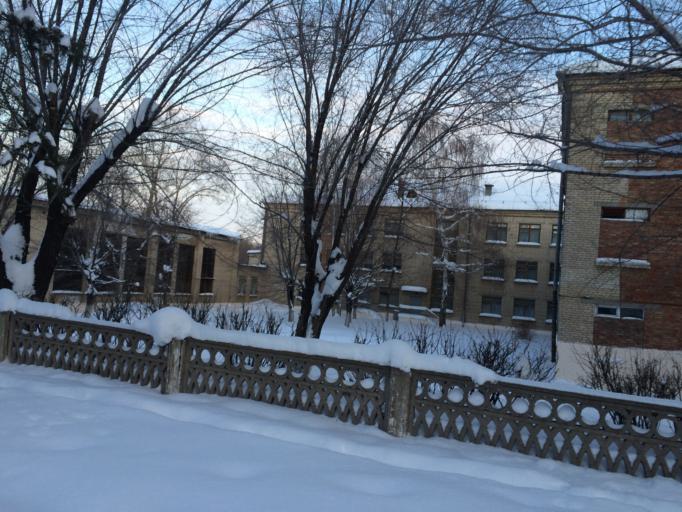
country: RU
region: Chelyabinsk
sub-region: Gorod Magnitogorsk
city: Magnitogorsk
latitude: 53.4009
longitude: 58.9718
